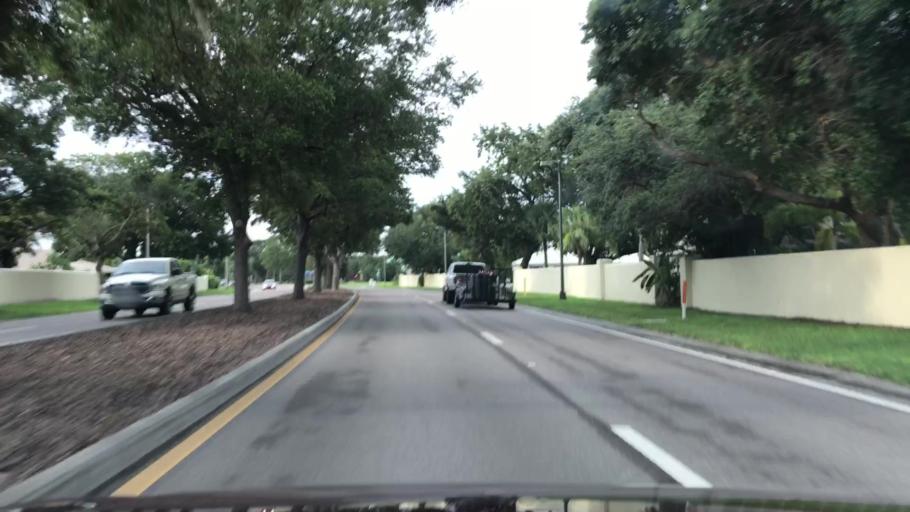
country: US
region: Florida
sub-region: Sarasota County
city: Plantation
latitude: 27.0685
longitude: -82.3895
